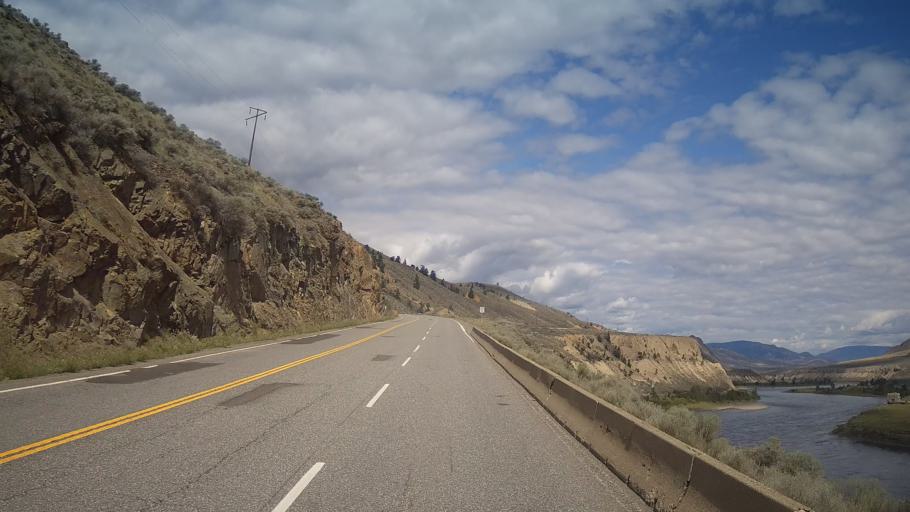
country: CA
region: British Columbia
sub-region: Thompson-Nicola Regional District
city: Ashcroft
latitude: 50.5514
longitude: -121.2962
